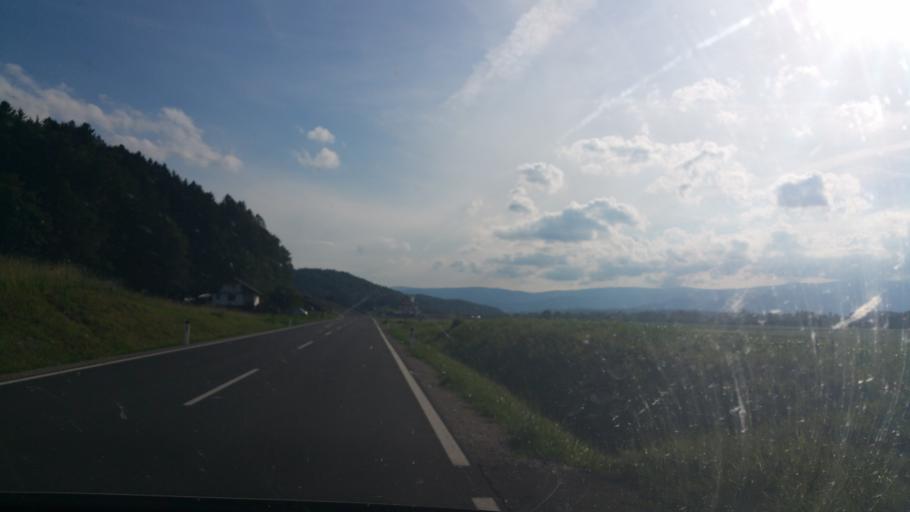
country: AT
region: Styria
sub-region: Politischer Bezirk Leibnitz
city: Gleinstatten
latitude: 46.7451
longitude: 15.3713
